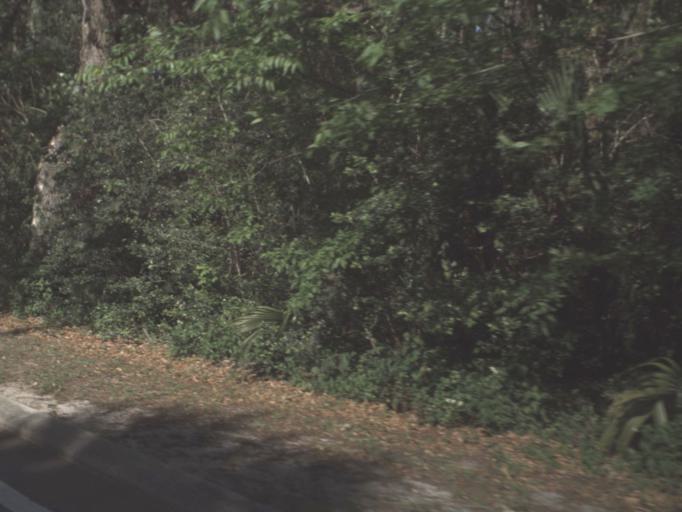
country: US
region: Florida
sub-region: Flagler County
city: Palm Coast
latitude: 29.5608
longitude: -81.1919
